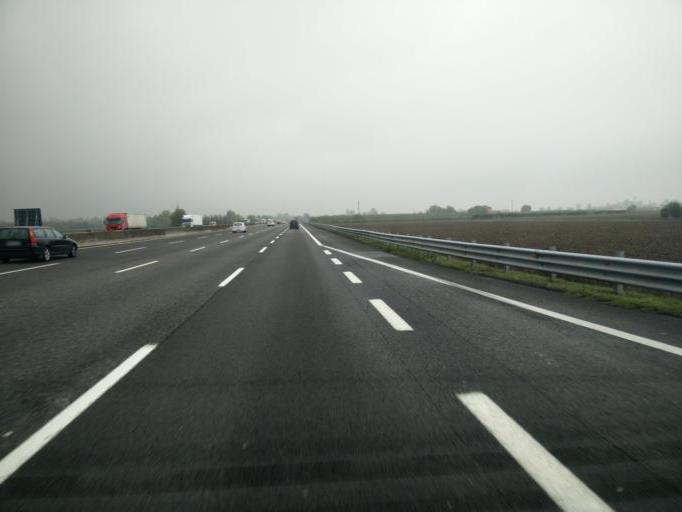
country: IT
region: Emilia-Romagna
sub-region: Provincia di Modena
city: Piumazzo
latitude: 44.5604
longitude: 11.0559
